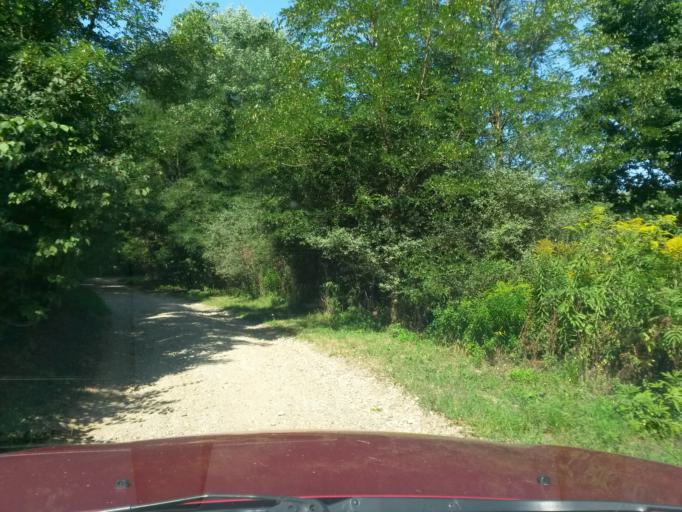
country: HU
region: Borsod-Abauj-Zemplen
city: Gonc
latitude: 48.5232
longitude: 21.2008
